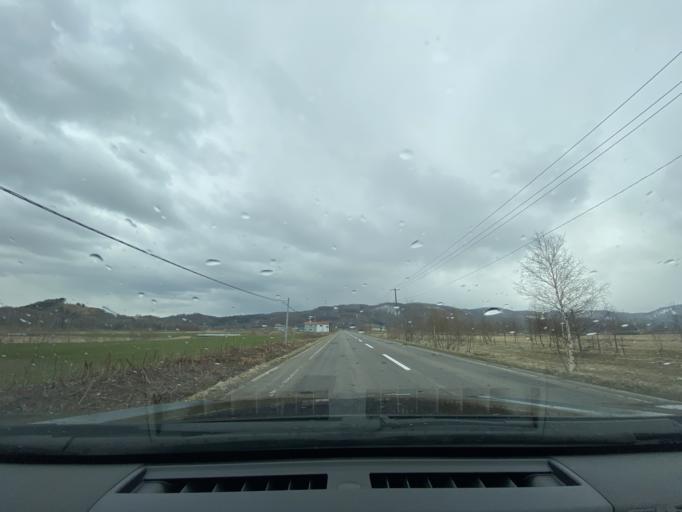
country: JP
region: Hokkaido
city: Nayoro
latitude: 44.1709
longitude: 142.2553
